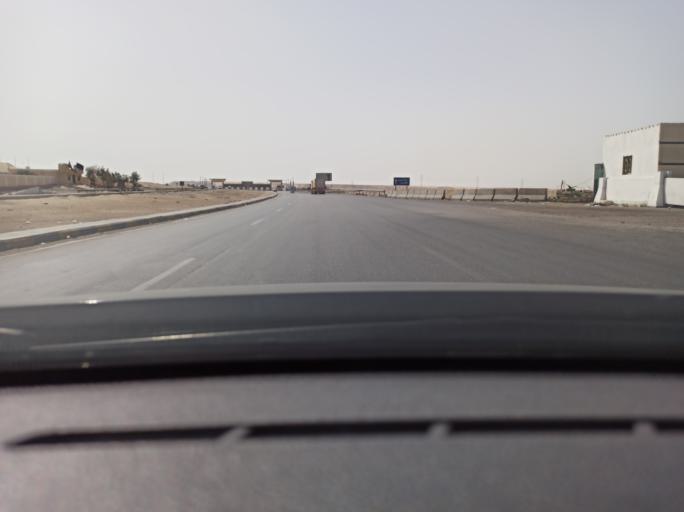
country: EG
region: Muhafazat al Qahirah
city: Halwan
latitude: 29.7083
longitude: 31.4093
